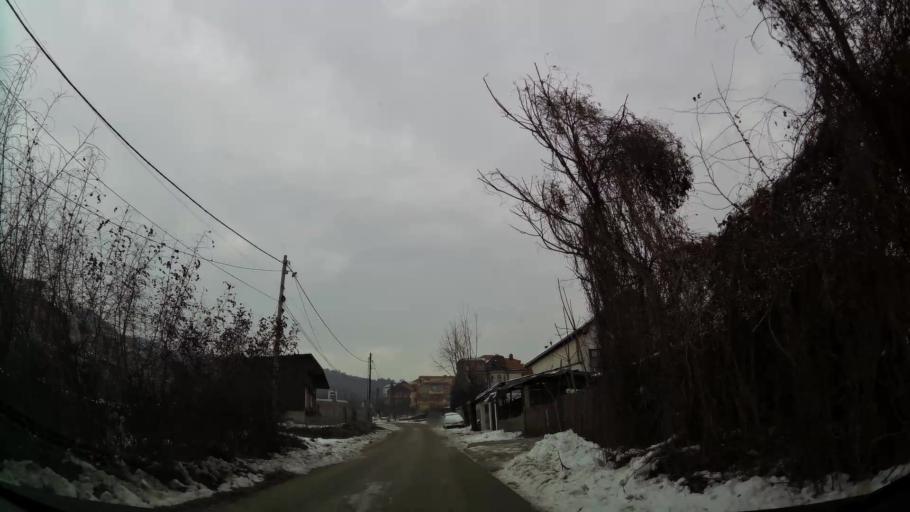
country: MK
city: Kondovo
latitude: 42.0128
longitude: 21.3058
